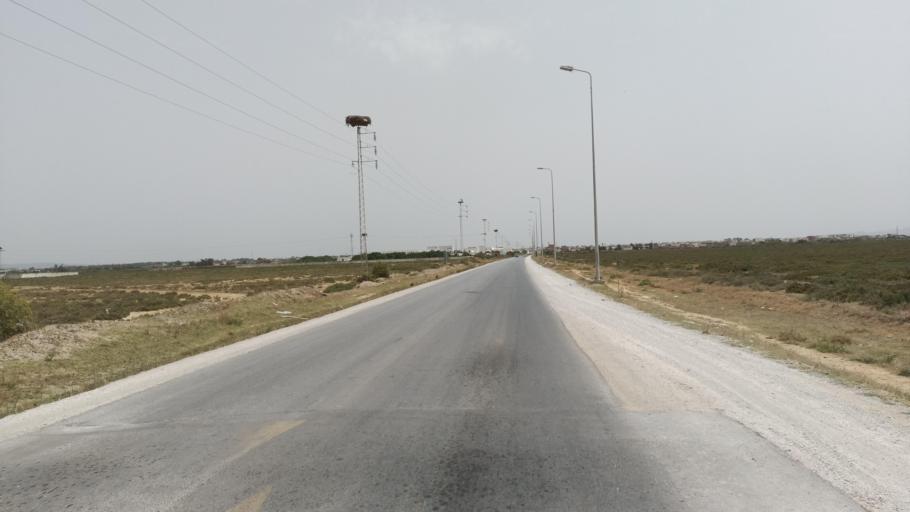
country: TN
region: Nabul
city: Manzil Bu Zalafah
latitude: 36.7170
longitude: 10.4775
